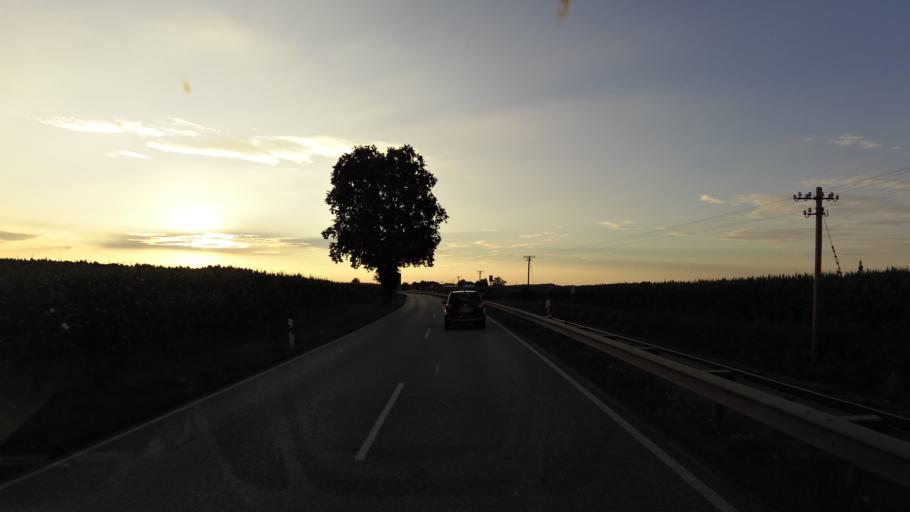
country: DE
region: Bavaria
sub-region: Upper Bavaria
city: Nussdorf
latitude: 47.9303
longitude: 12.5990
